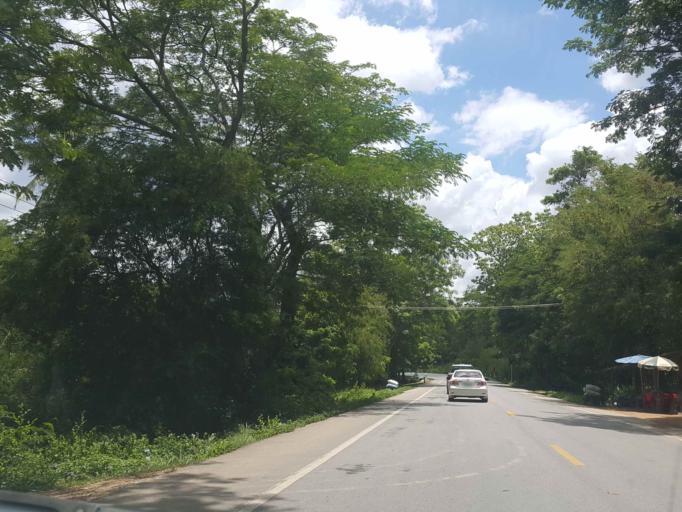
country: TH
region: Nan
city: Wiang Sa
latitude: 18.5168
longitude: 100.5967
